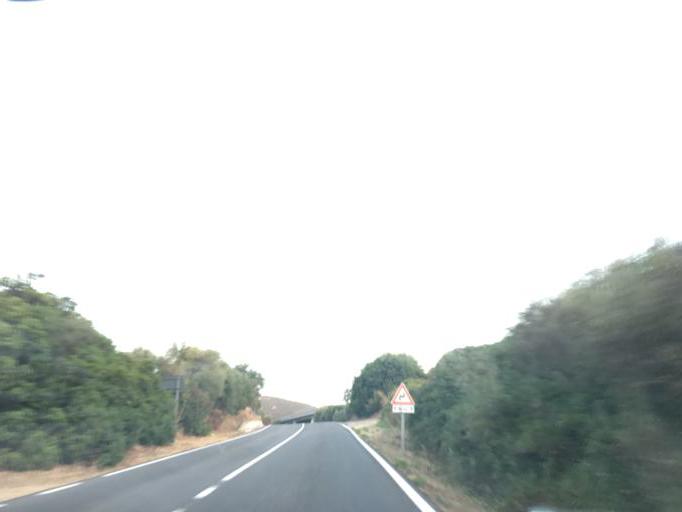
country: IT
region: Sardinia
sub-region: Provincia di Olbia-Tempio
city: San Teodoro
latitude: 40.7383
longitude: 9.6468
